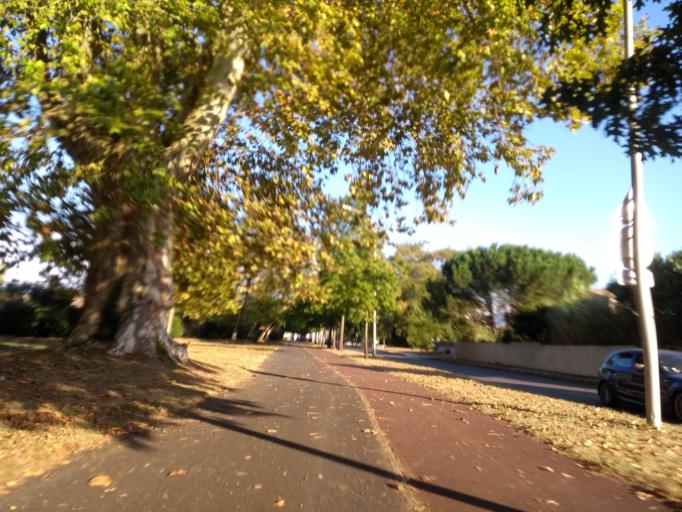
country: FR
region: Aquitaine
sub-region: Departement de la Gironde
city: Pessac
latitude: 44.8033
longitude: -0.6659
